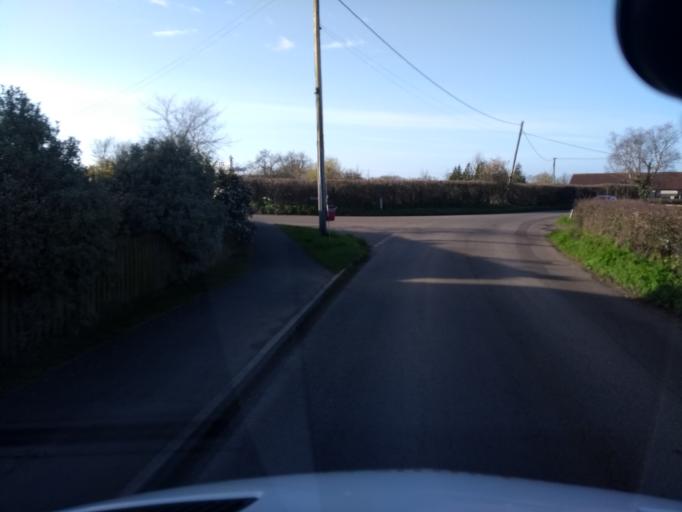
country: GB
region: England
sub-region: Somerset
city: Wedmore
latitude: 51.1771
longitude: -2.8107
